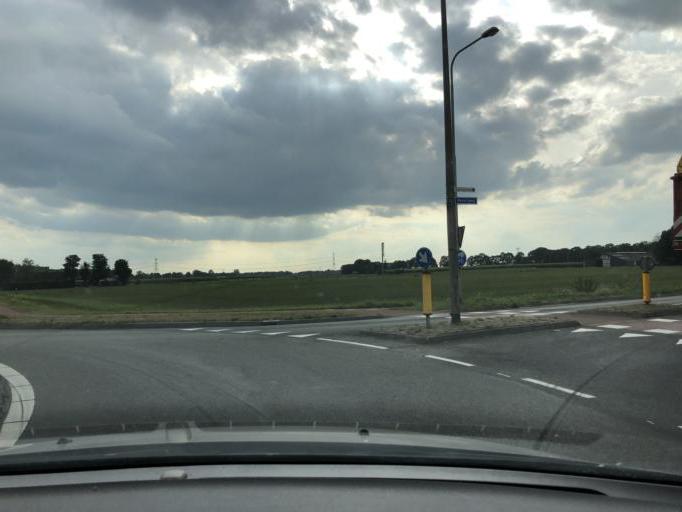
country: NL
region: Overijssel
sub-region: Gemeente Hardenberg
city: Hardenberg
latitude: 52.6216
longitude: 6.5508
